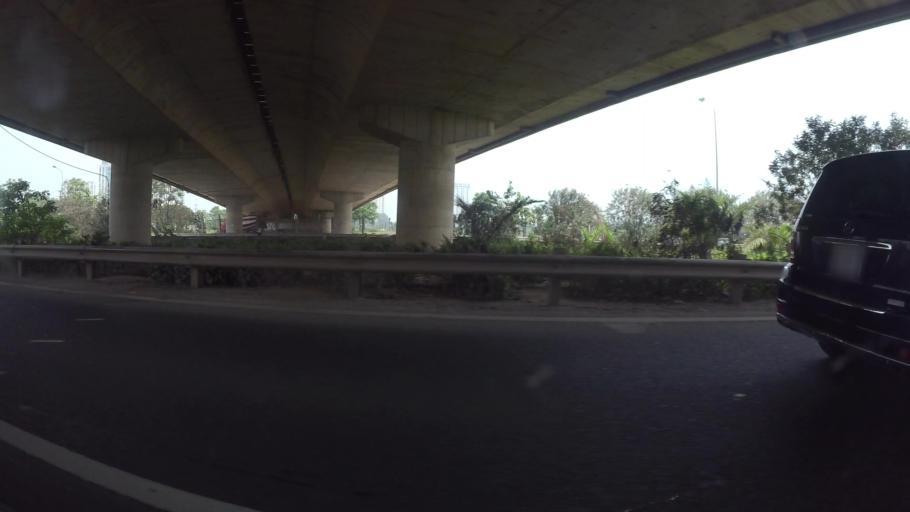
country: VN
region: Ha Noi
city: Cau Dien
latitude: 21.0092
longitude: 105.7480
